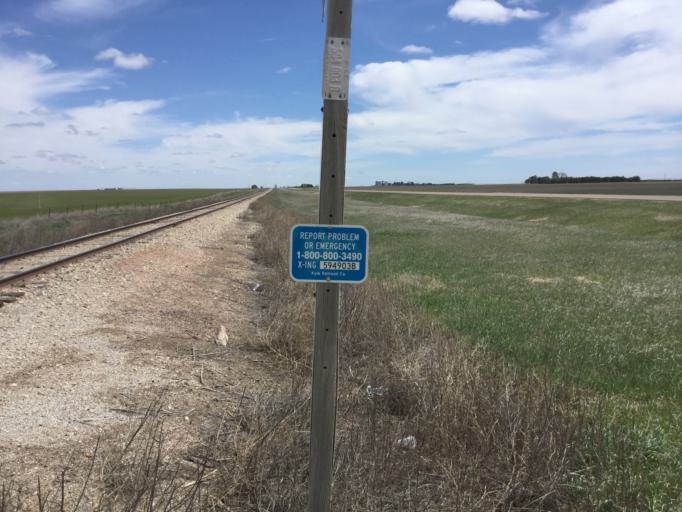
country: US
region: Kansas
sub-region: Sherman County
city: Goodland
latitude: 39.3402
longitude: -101.6514
